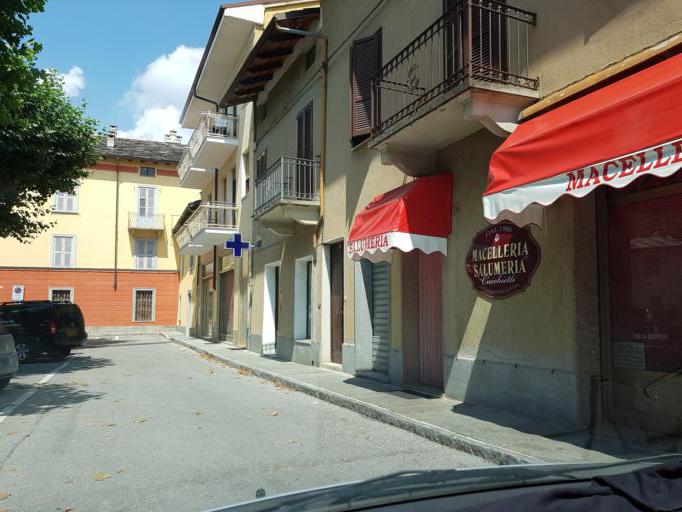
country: IT
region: Piedmont
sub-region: Provincia di Cuneo
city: Dronero
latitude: 44.4679
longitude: 7.3610
